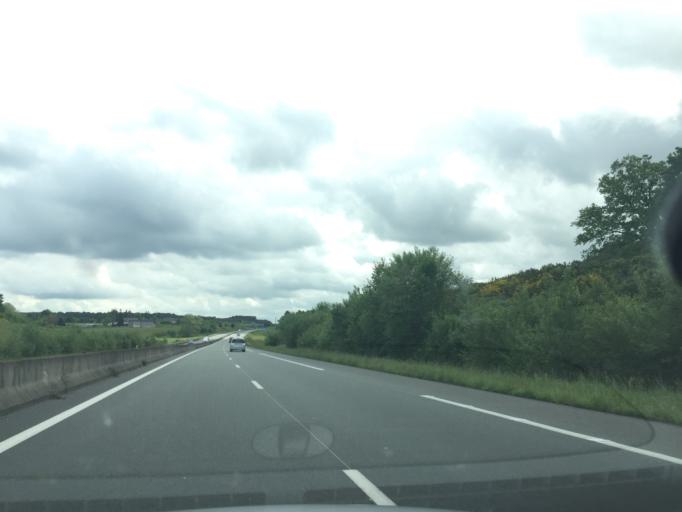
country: FR
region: Pays de la Loire
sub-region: Departement de la Sarthe
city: Mayet
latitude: 47.7746
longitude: 0.3131
